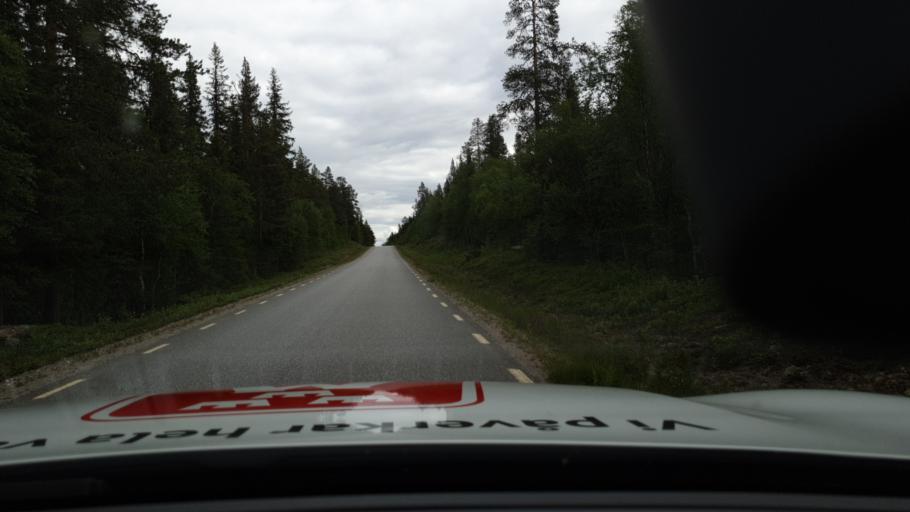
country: SE
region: Norrbotten
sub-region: Arjeplogs Kommun
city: Arjeplog
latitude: 66.8941
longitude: 17.9313
